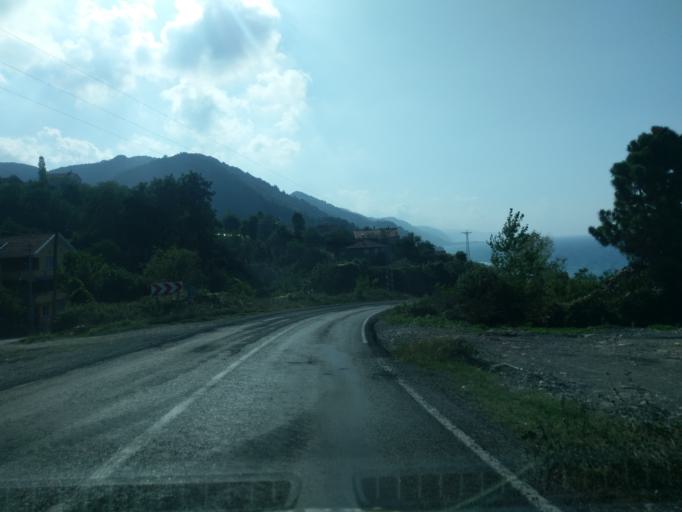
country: TR
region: Sinop
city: Ayancik
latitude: 41.9404
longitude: 34.6656
